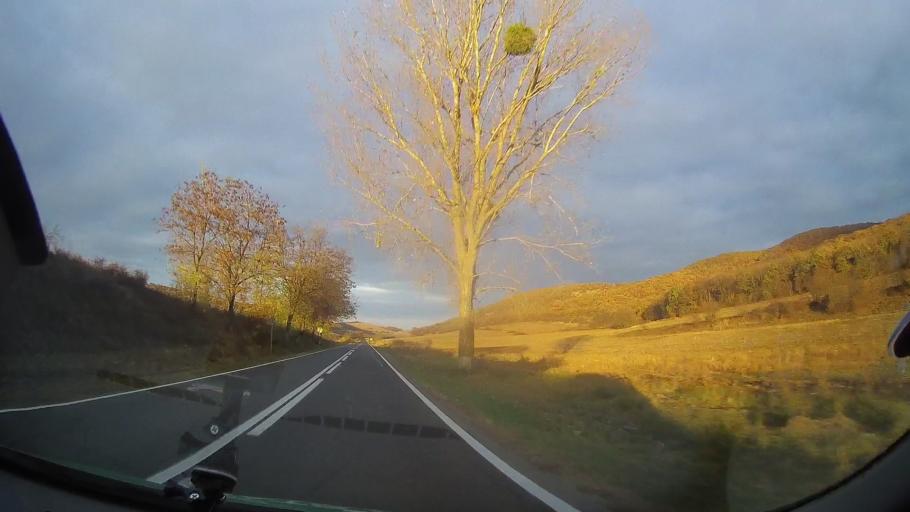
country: RO
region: Tulcea
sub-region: Comuna Ciucurova
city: Ciucurova
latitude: 44.9523
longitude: 28.5119
